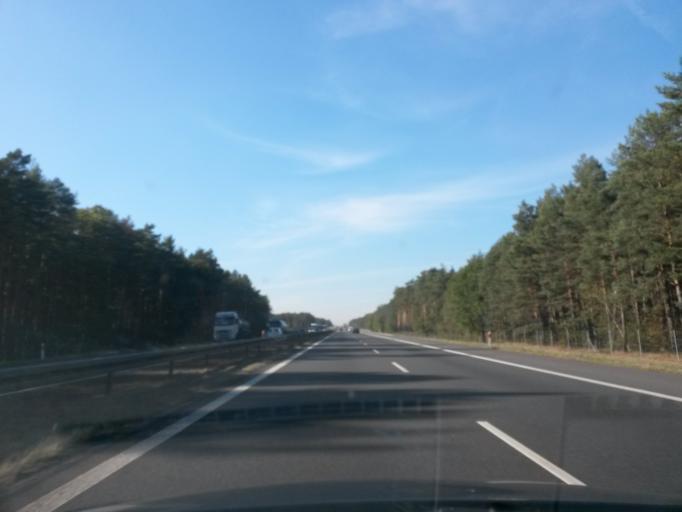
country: PL
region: Opole Voivodeship
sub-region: Powiat opolski
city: Komprachcice
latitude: 50.6115
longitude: 17.7760
